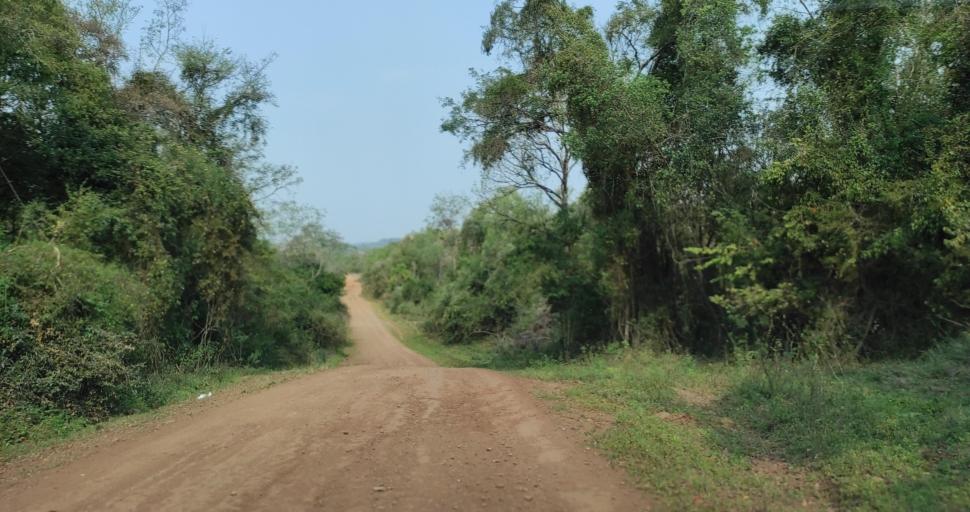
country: AR
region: Misiones
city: Cerro Cora
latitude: -27.5356
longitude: -55.5887
